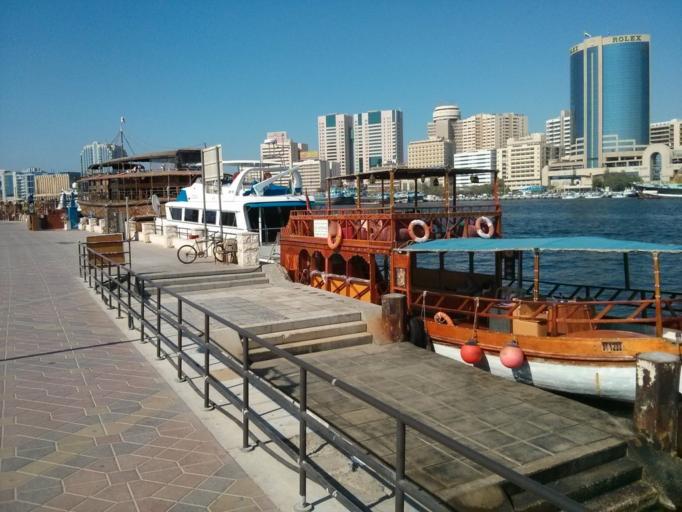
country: AE
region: Ash Shariqah
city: Sharjah
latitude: 25.2611
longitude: 55.3091
